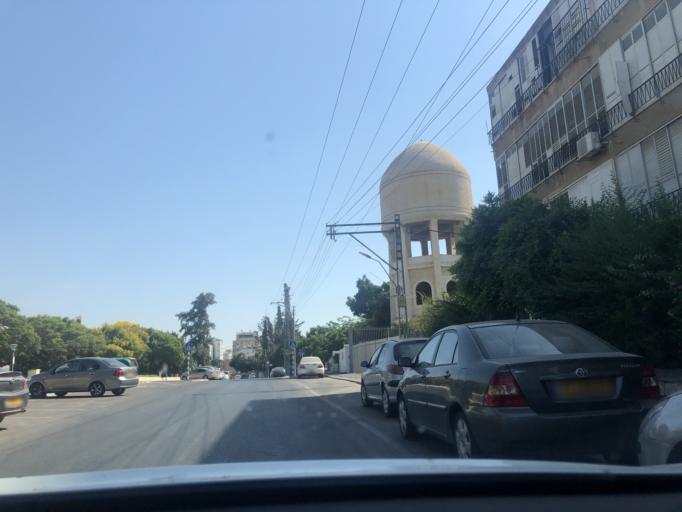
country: IL
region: Central District
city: Lod
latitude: 31.9531
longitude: 34.8940
